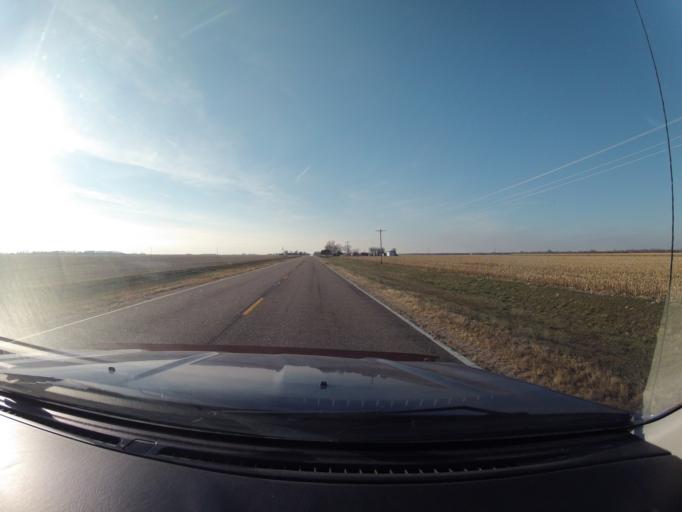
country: US
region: Nebraska
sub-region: Buffalo County
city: Kearney
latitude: 40.6410
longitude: -98.9761
